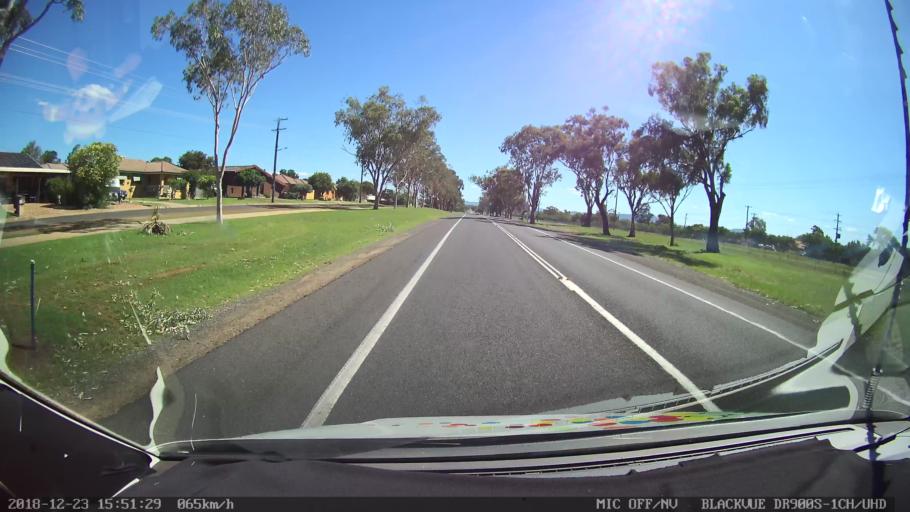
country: AU
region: New South Wales
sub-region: Tamworth Municipality
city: South Tamworth
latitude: -31.1131
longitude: 150.8957
